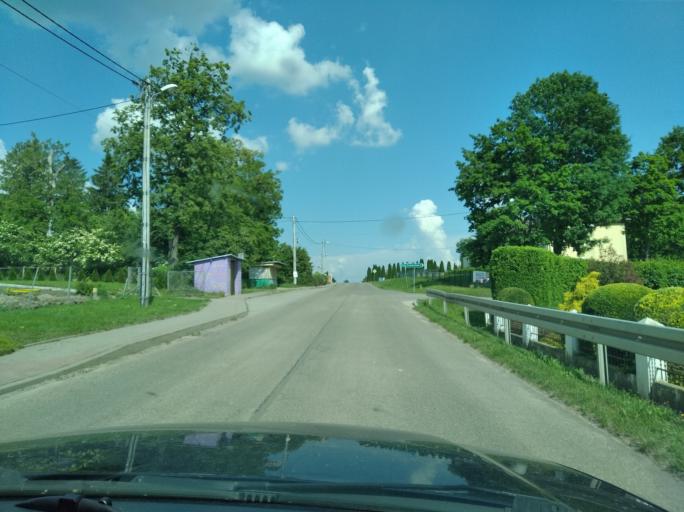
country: PL
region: Subcarpathian Voivodeship
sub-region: Powiat jaroslawski
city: Ostrow
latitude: 49.9403
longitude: 22.7389
